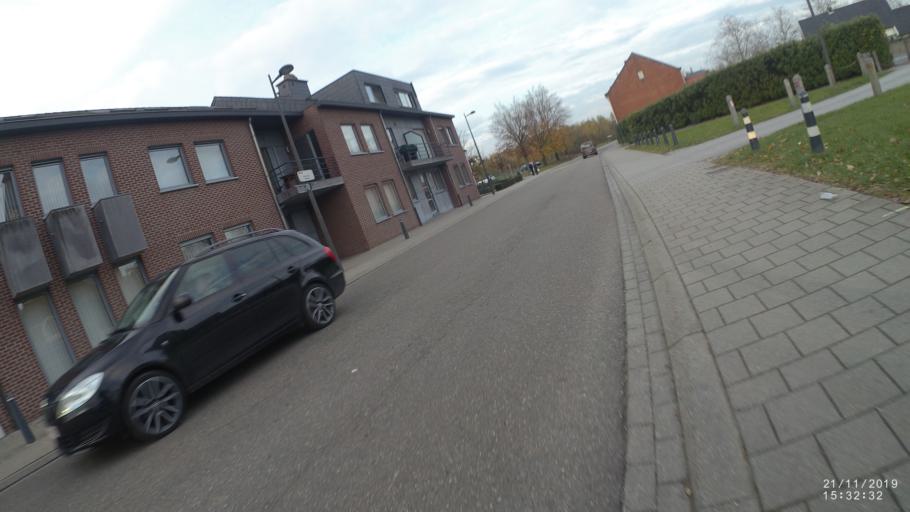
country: BE
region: Flanders
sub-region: Provincie Limburg
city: Hasselt
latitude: 50.9442
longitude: 5.3053
